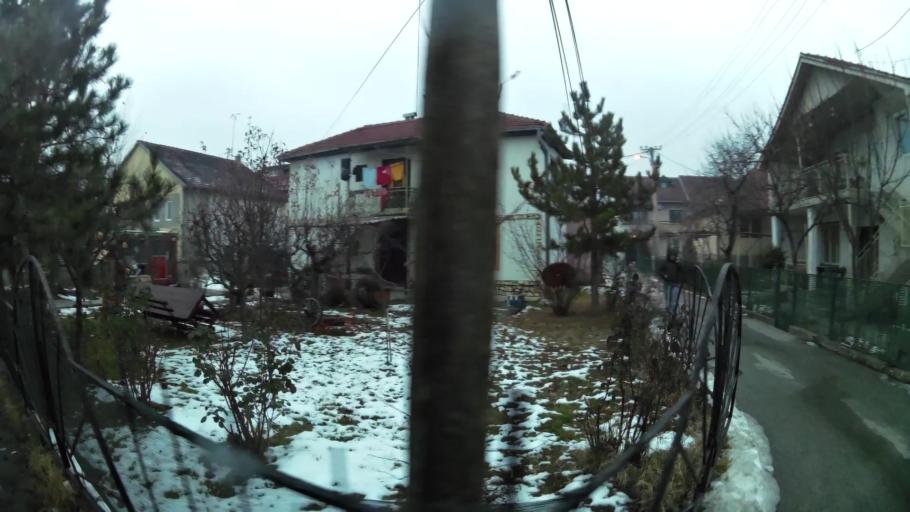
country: MK
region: Kisela Voda
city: Usje
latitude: 41.9748
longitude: 21.4832
